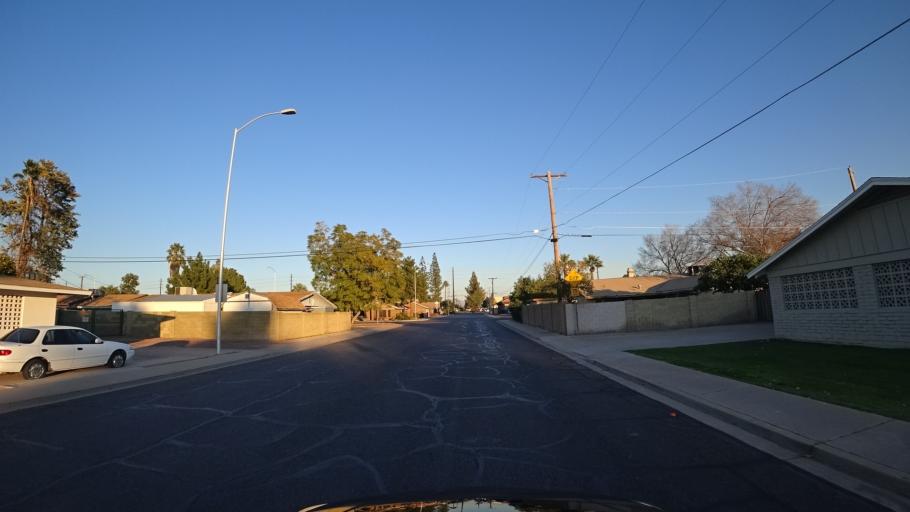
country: US
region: Arizona
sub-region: Maricopa County
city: Mesa
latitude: 33.4260
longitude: -111.8069
